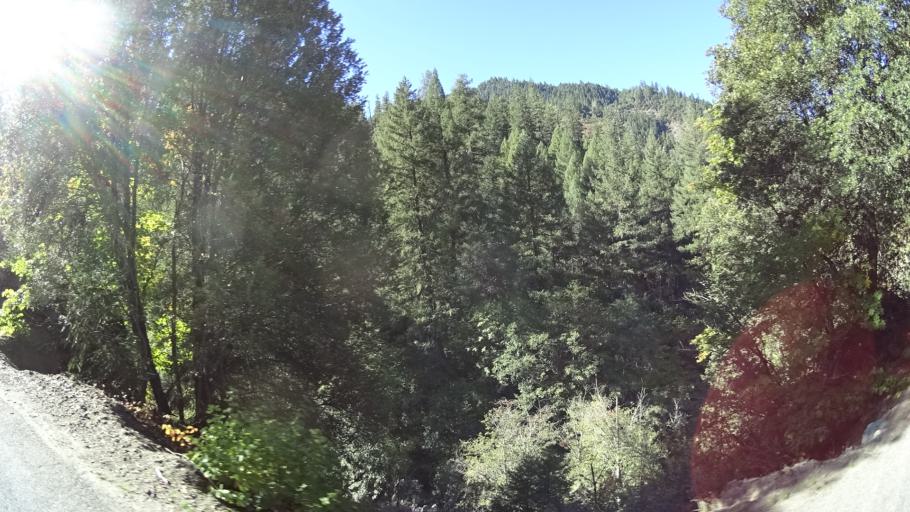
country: US
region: California
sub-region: Humboldt County
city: Willow Creek
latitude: 41.1454
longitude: -123.1943
